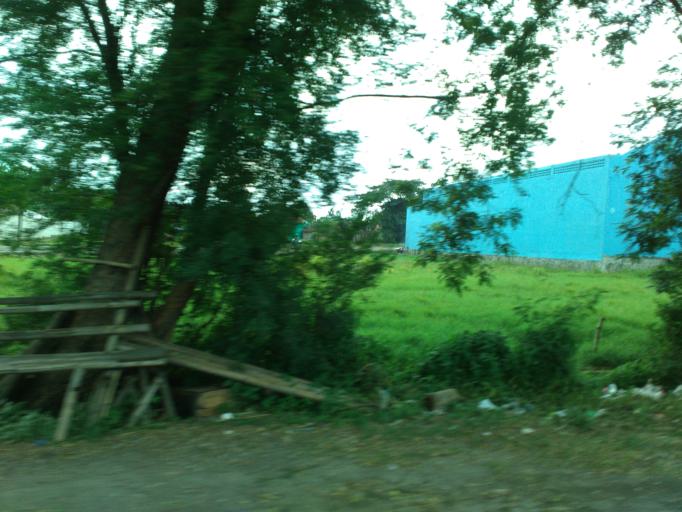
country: ID
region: Central Java
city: Ceper
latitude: -7.6680
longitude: 110.6606
